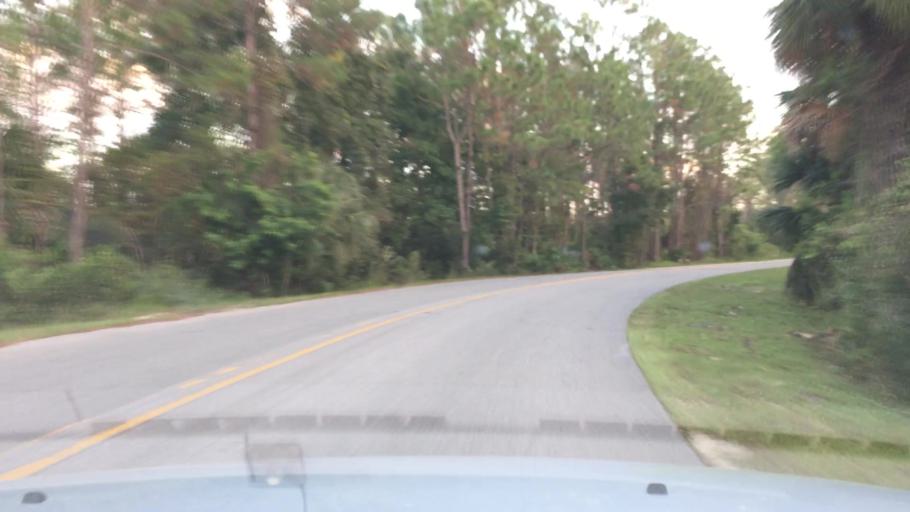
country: US
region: Florida
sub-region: Volusia County
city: Ormond Beach
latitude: 29.2843
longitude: -81.1239
